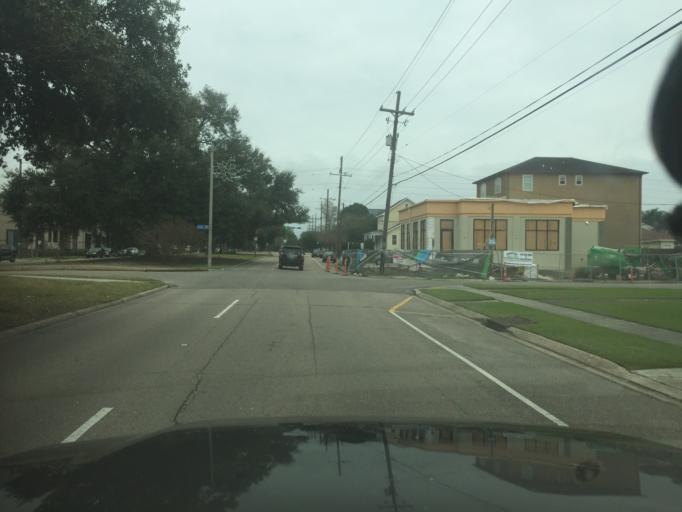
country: US
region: Louisiana
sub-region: Jefferson Parish
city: Metairie
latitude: 30.0048
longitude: -90.1097
